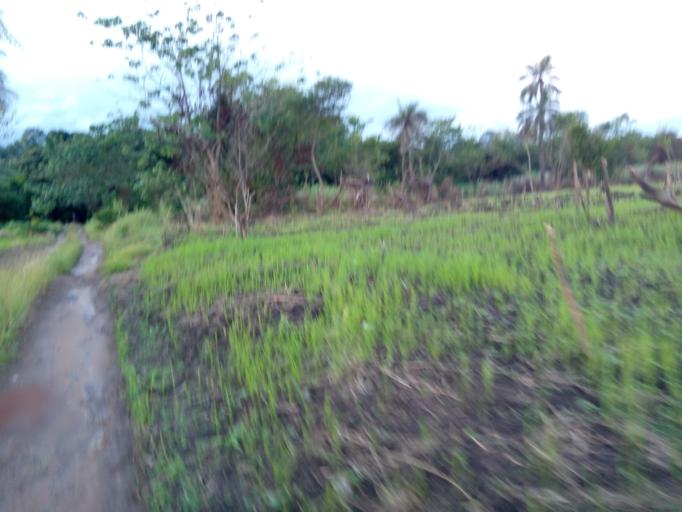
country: SL
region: Eastern Province
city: Buedu
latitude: 8.4923
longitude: -10.3440
